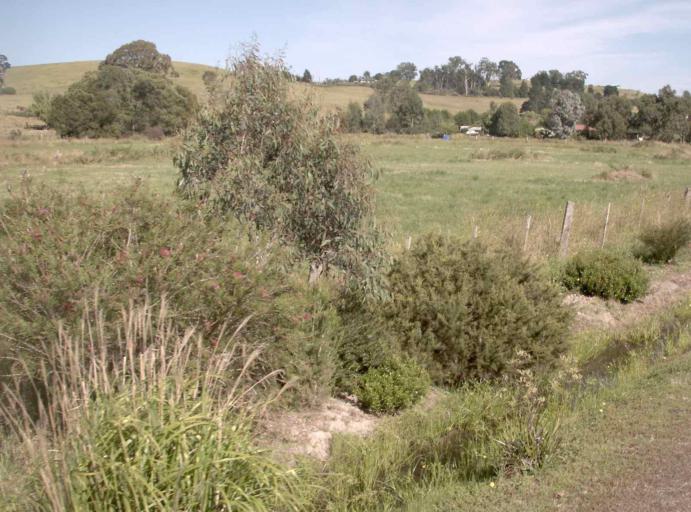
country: AU
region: Victoria
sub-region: East Gippsland
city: Bairnsdale
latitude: -37.7287
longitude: 147.8091
